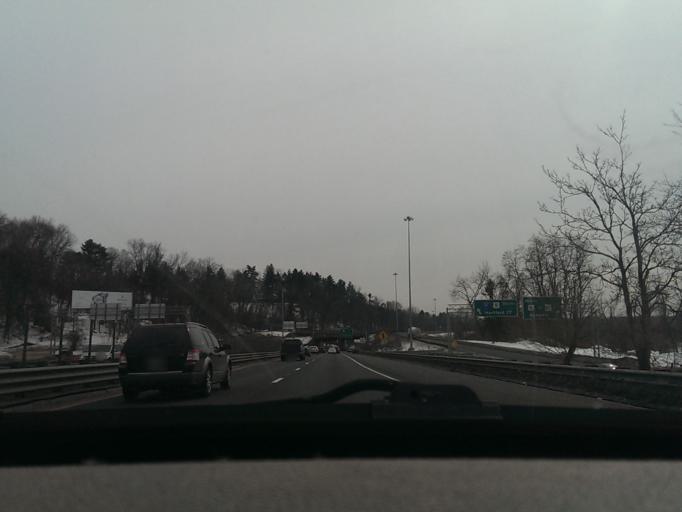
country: US
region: Massachusetts
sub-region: Hampden County
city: Springfield
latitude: 42.0855
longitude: -72.5801
